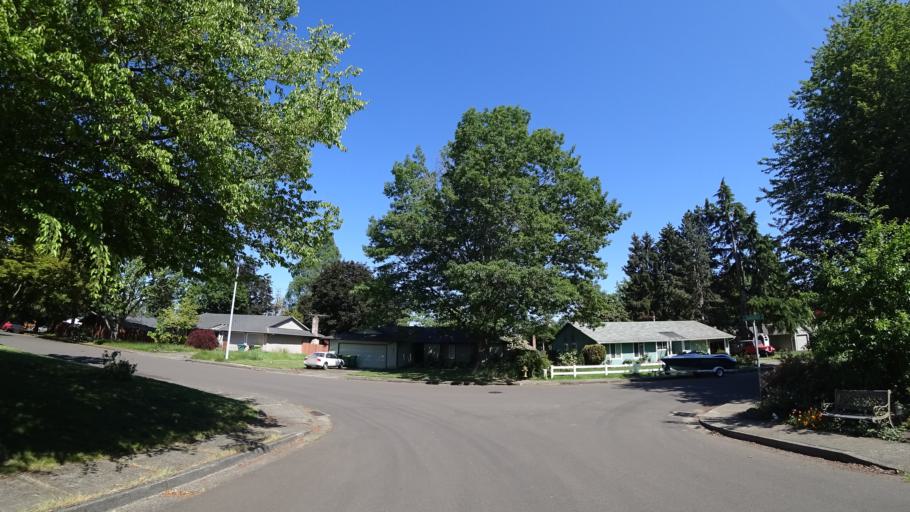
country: US
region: Oregon
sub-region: Washington County
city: Beaverton
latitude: 45.4578
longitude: -122.8000
